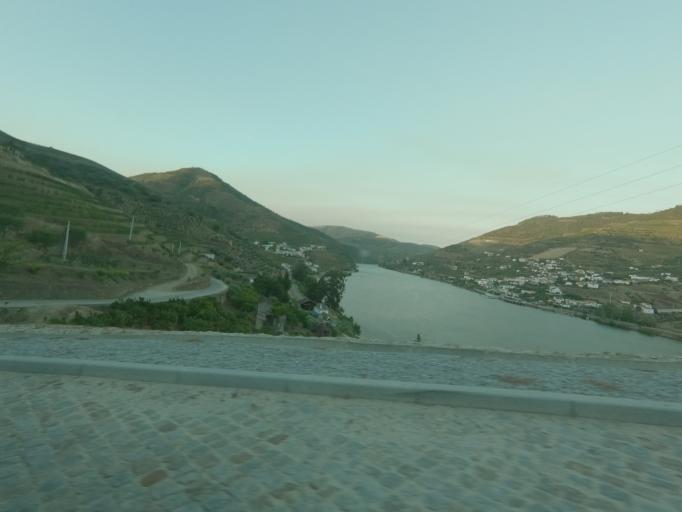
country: PT
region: Viseu
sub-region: Armamar
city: Armamar
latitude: 41.1508
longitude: -7.6904
